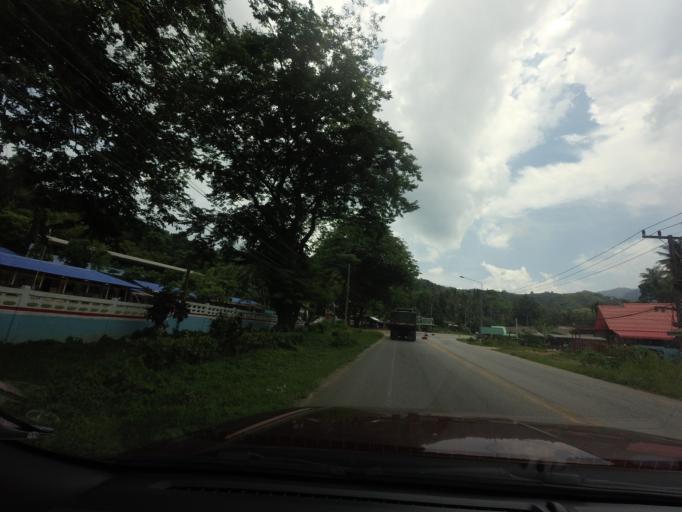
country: TH
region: Yala
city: Than To
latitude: 6.0714
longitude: 101.1962
